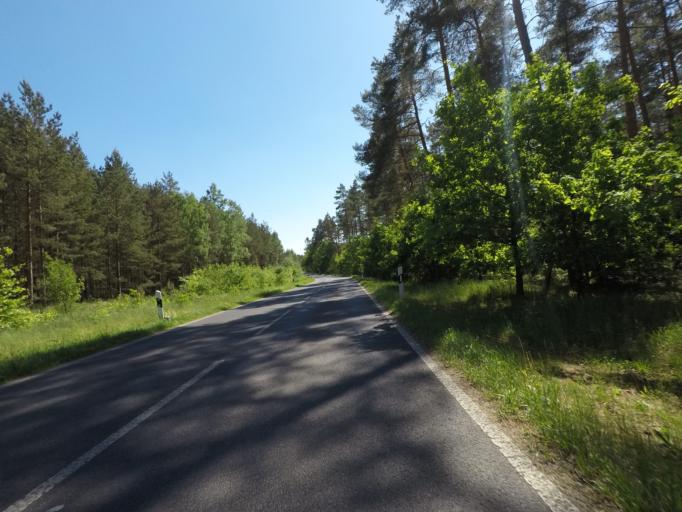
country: DE
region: Brandenburg
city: Eberswalde
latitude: 52.8250
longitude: 13.7704
